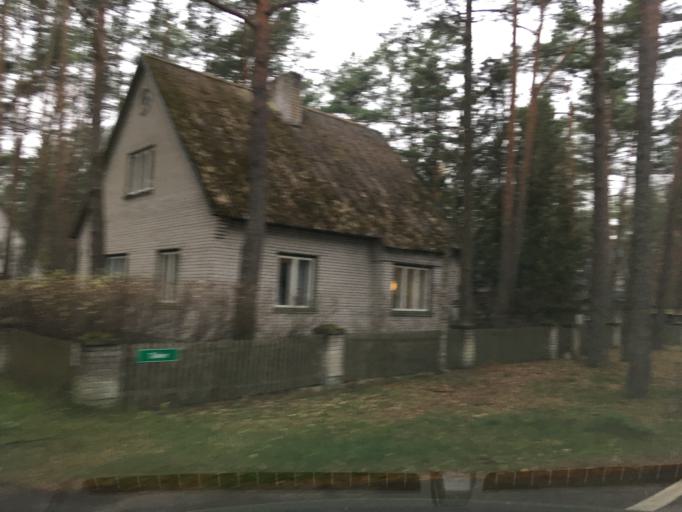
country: EE
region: Harju
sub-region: Saku vald
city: Saku
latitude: 59.3719
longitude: 24.6955
